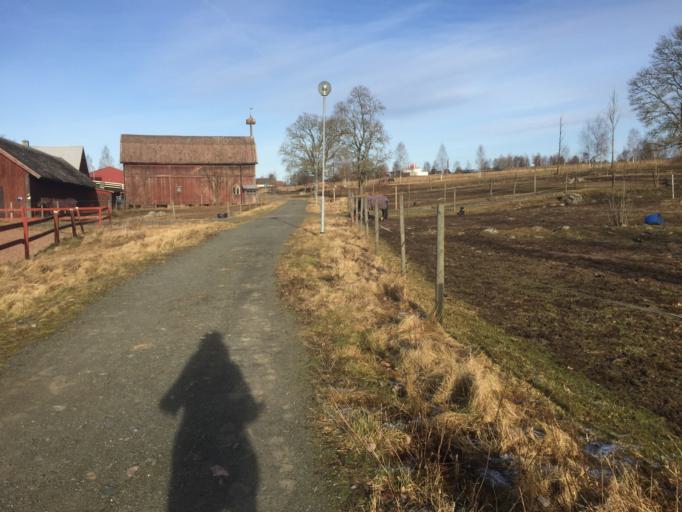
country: SE
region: Joenkoeping
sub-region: Aneby Kommun
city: Aneby
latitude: 57.8252
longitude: 14.8155
